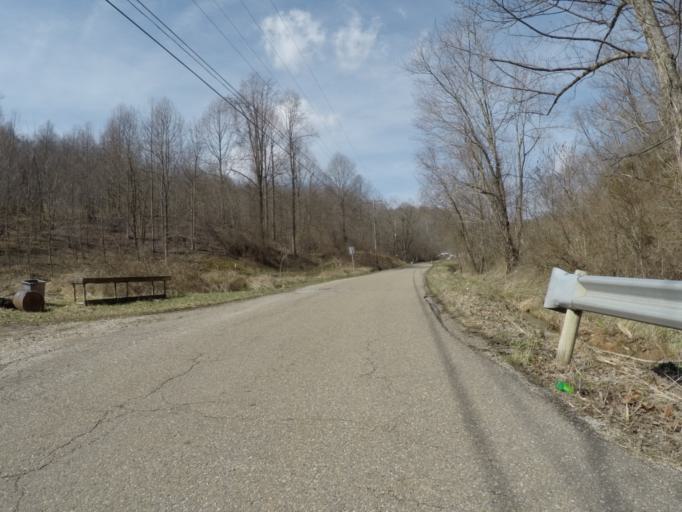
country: US
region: Ohio
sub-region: Lawrence County
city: Burlington
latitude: 38.4804
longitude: -82.5284
